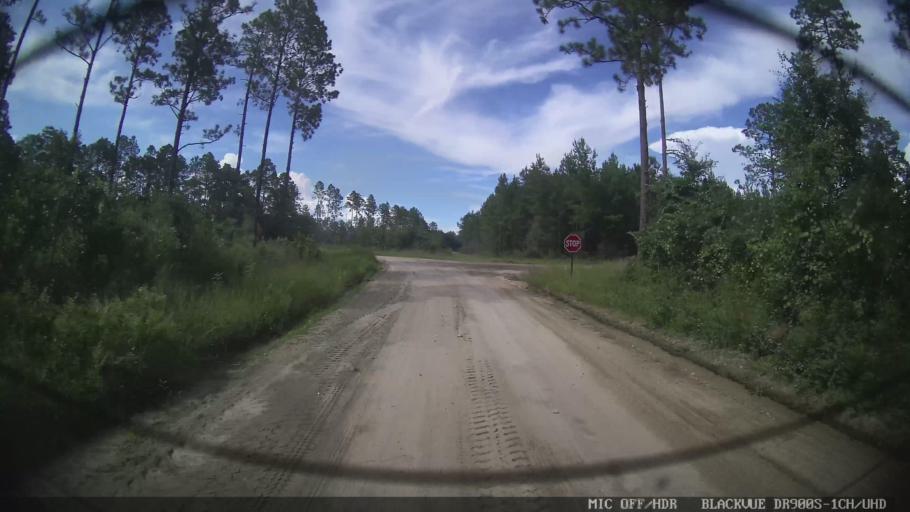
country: US
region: Georgia
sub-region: Echols County
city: Statenville
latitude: 30.6231
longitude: -83.1993
